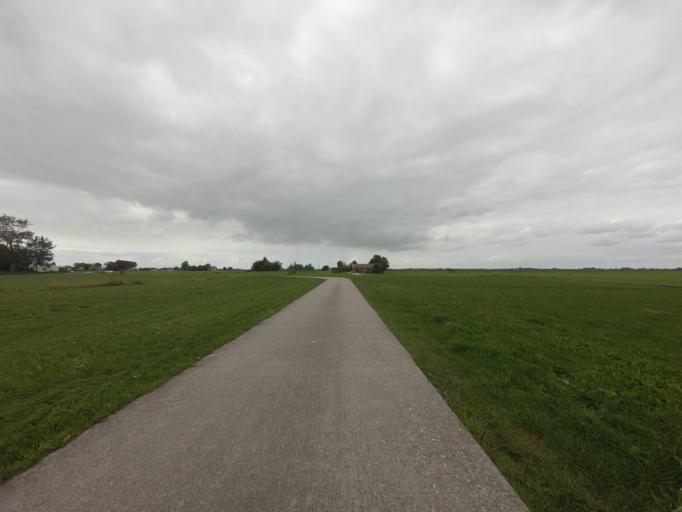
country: NL
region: Friesland
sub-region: Sudwest Fryslan
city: Workum
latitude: 52.9887
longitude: 5.5174
